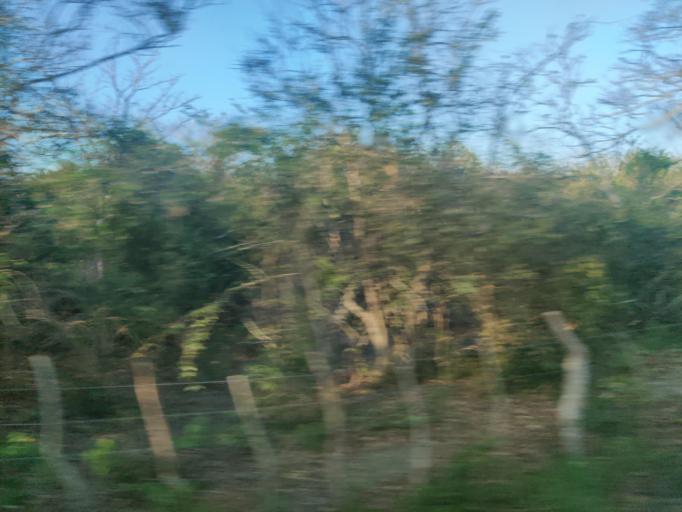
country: CO
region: Atlantico
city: Piojo
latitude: 10.7477
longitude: -75.2462
